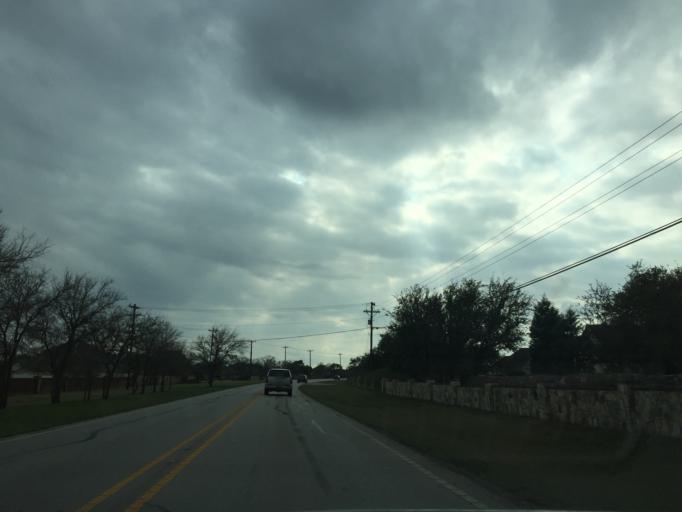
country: US
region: Texas
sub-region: Hays County
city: Dripping Springs
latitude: 30.1429
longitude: -97.9929
